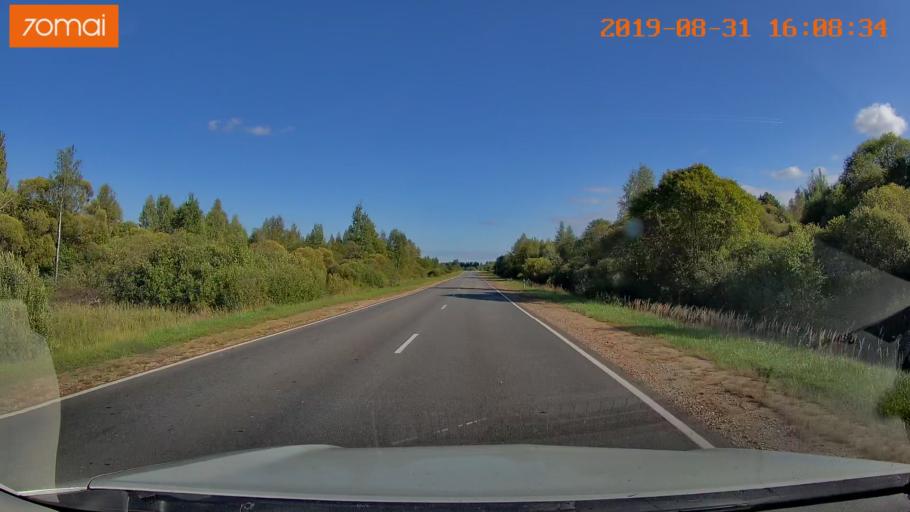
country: RU
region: Kaluga
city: Yukhnov
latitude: 54.5954
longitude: 35.3780
